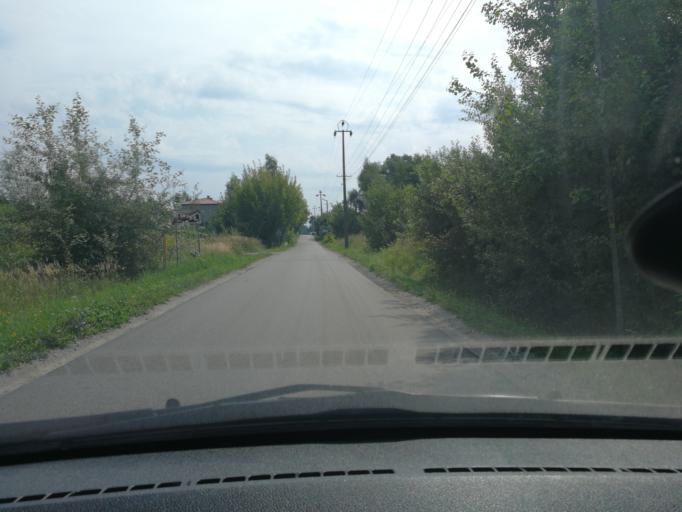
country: PL
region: Lodz Voivodeship
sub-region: Skierniewice
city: Skierniewice
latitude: 51.9718
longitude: 20.1138
